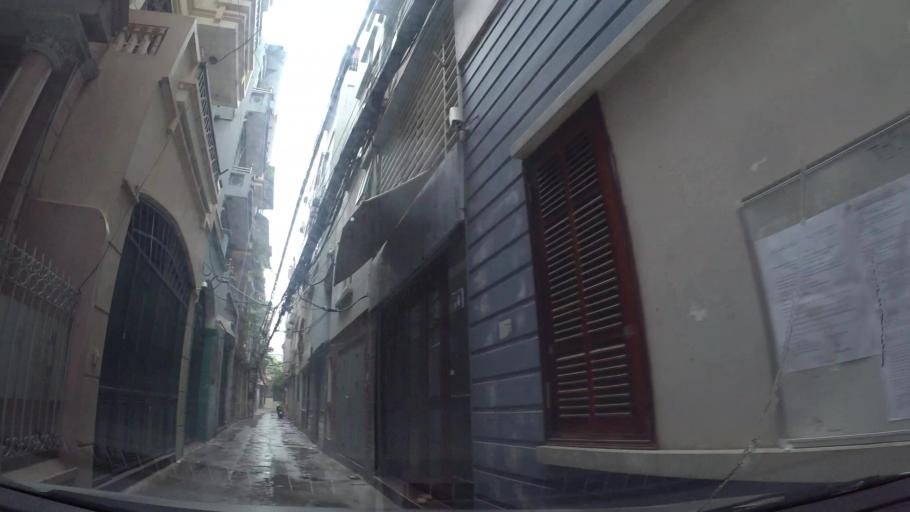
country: VN
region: Ha Noi
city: Cau Giay
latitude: 21.0204
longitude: 105.7997
